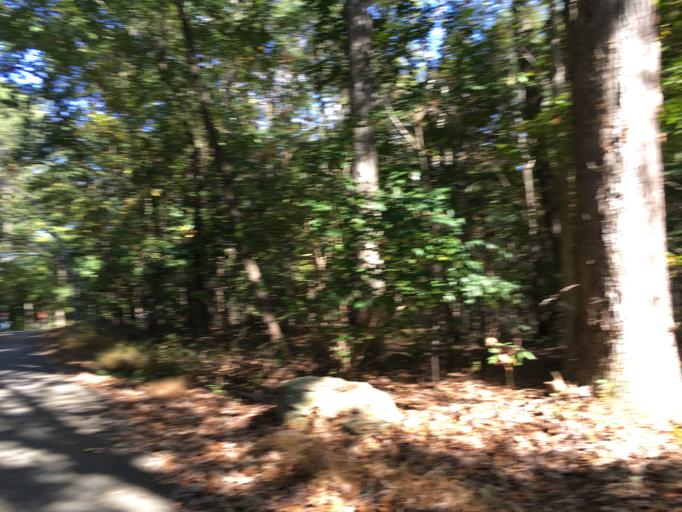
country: US
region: Pennsylvania
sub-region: York County
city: Yorklyn
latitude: 40.0114
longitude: -76.6533
